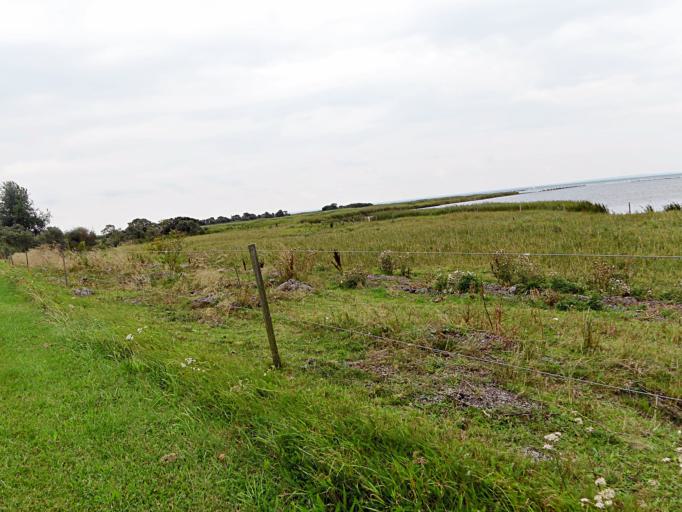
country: DK
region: Capital Region
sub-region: Fredensborg Kommune
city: Niva
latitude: 55.9271
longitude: 12.5186
